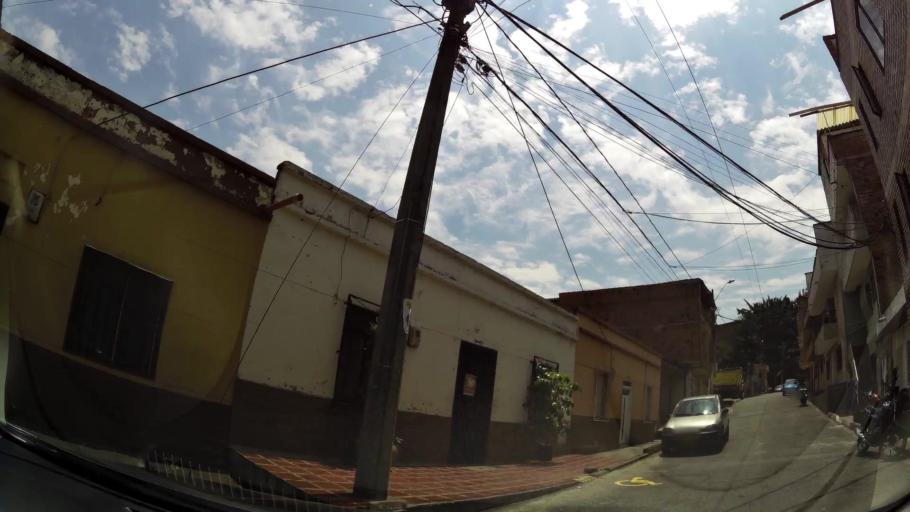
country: CO
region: Antioquia
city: Medellin
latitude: 6.2532
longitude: -75.6190
